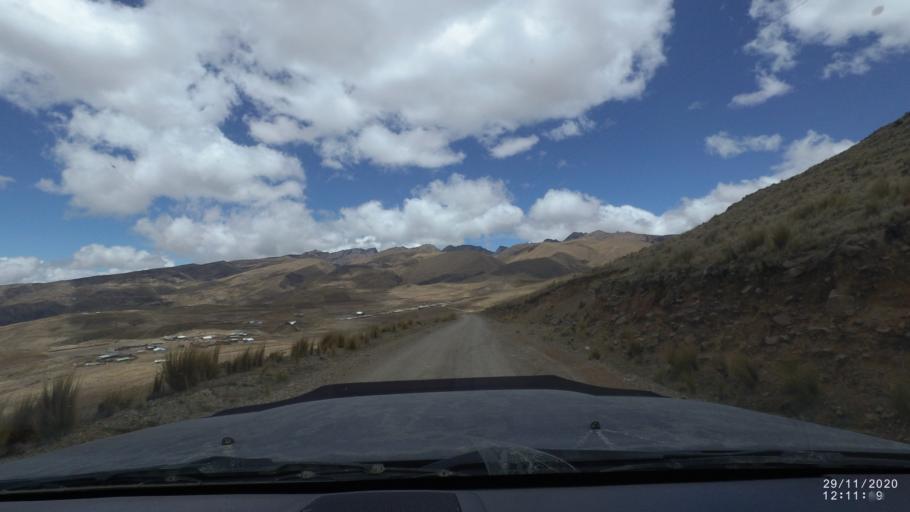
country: BO
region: Cochabamba
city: Cochabamba
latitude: -17.1200
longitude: -66.3057
